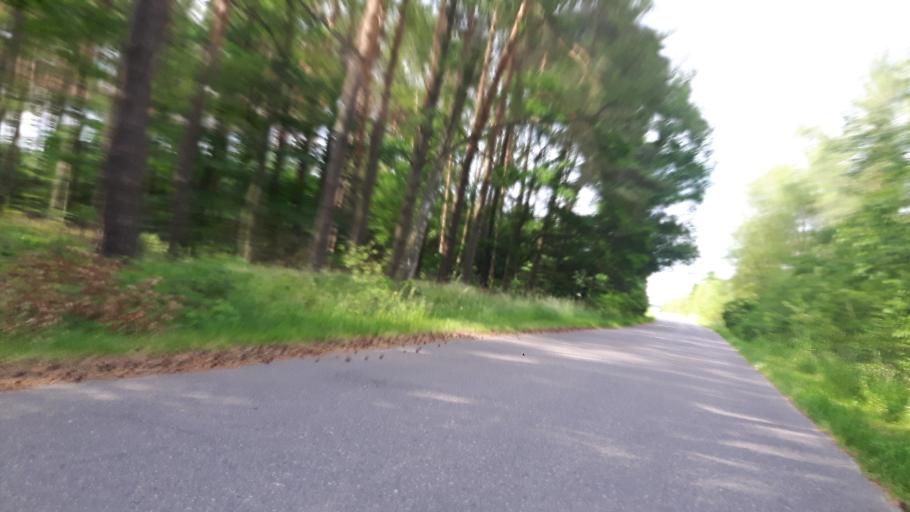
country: PL
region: West Pomeranian Voivodeship
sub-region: Powiat goleniowski
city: Nowogard
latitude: 53.8051
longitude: 15.1277
